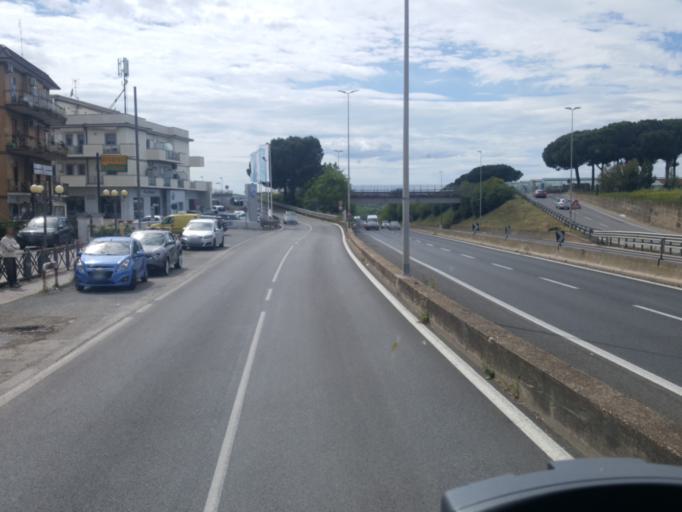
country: IT
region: Latium
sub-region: Citta metropolitana di Roma Capitale
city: La Massimina-Casal Lumbroso
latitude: 41.8816
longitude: 12.3487
